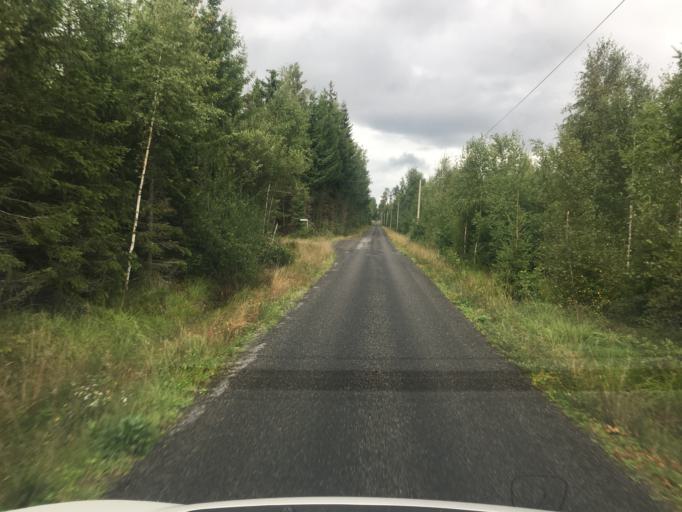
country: SE
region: Kronoberg
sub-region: Ljungby Kommun
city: Lagan
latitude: 56.9409
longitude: 14.0279
